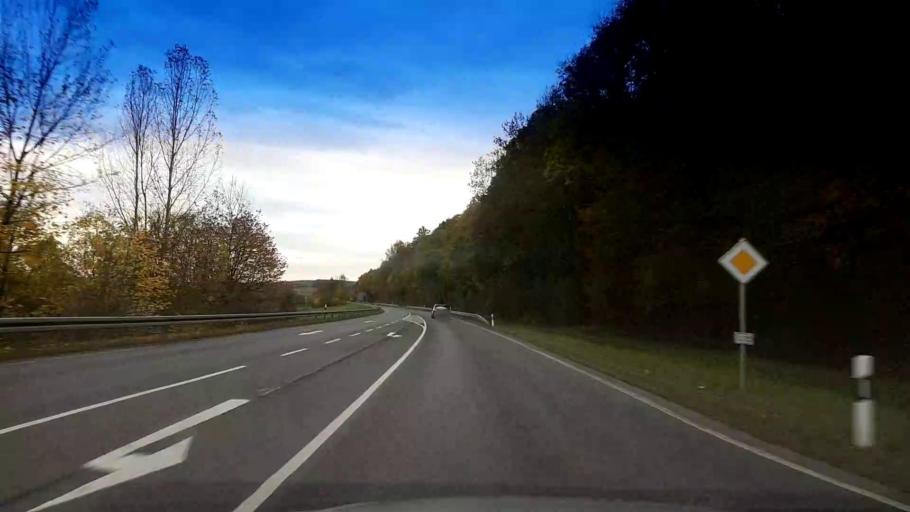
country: DE
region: Bavaria
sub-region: Regierungsbezirk Unterfranken
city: Stettfeld
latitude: 49.9438
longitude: 10.7271
